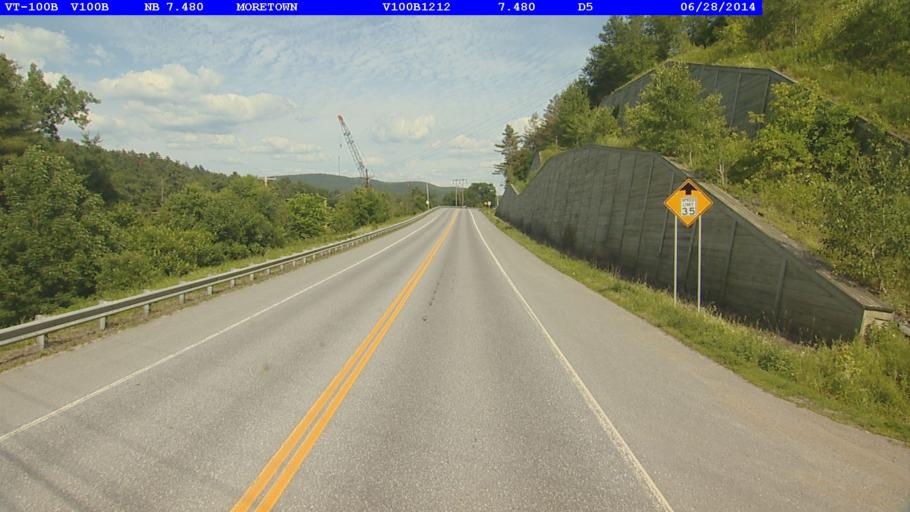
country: US
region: Vermont
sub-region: Washington County
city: Waterbury
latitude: 44.2920
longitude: -72.6857
